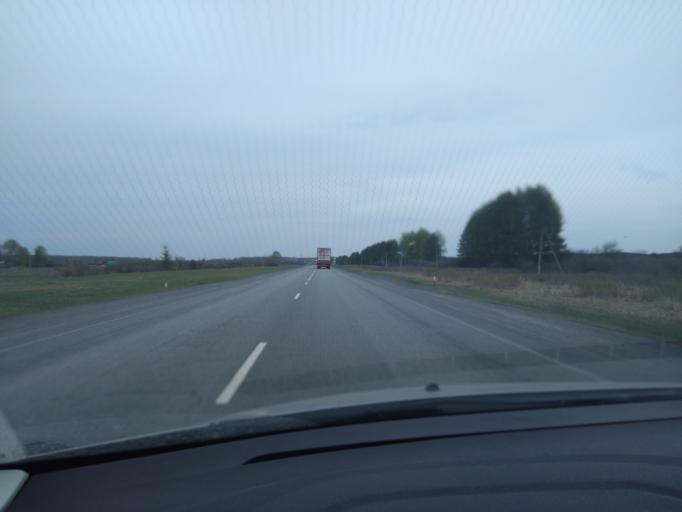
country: RU
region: Sverdlovsk
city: Troitskiy
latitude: 57.0774
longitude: 63.6250
